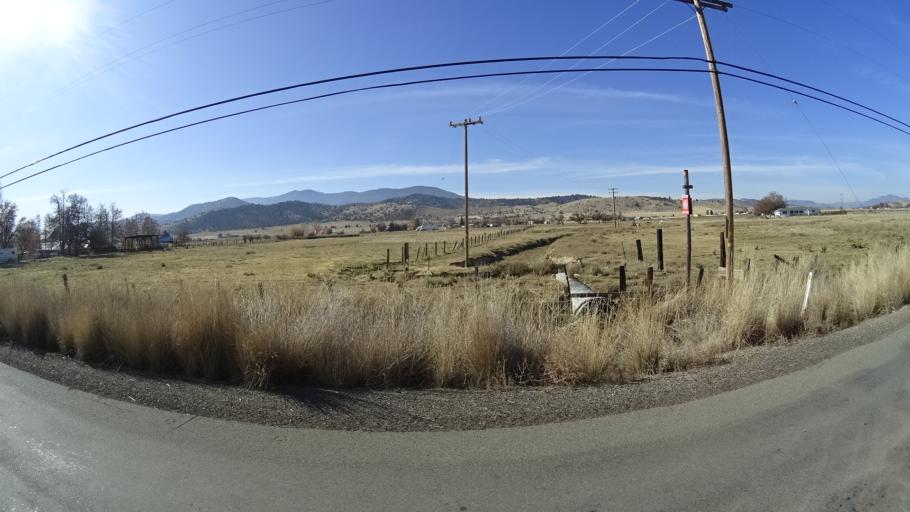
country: US
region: California
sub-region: Siskiyou County
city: Montague
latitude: 41.6334
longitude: -122.5218
